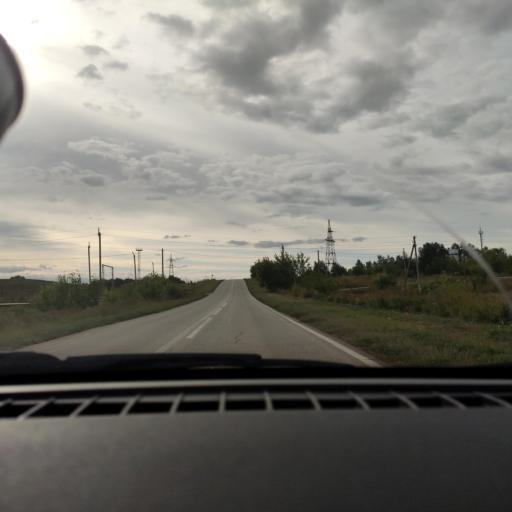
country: RU
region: Samara
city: Georgiyevka
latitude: 53.4204
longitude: 50.8480
